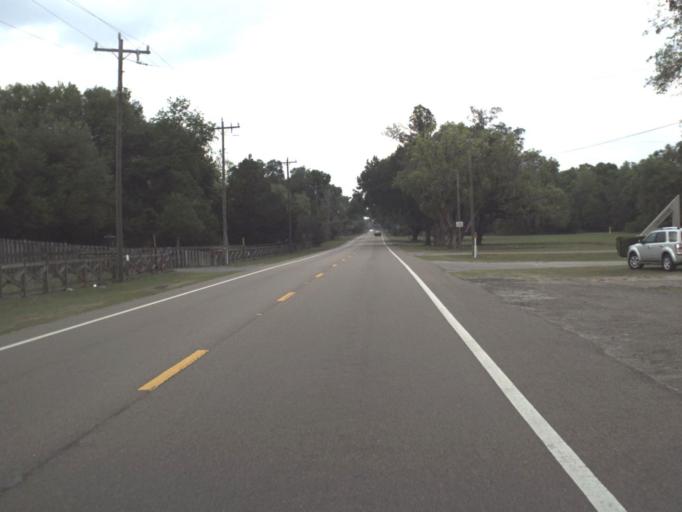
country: US
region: Florida
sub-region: Lake County
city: Umatilla
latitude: 28.9793
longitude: -81.6451
